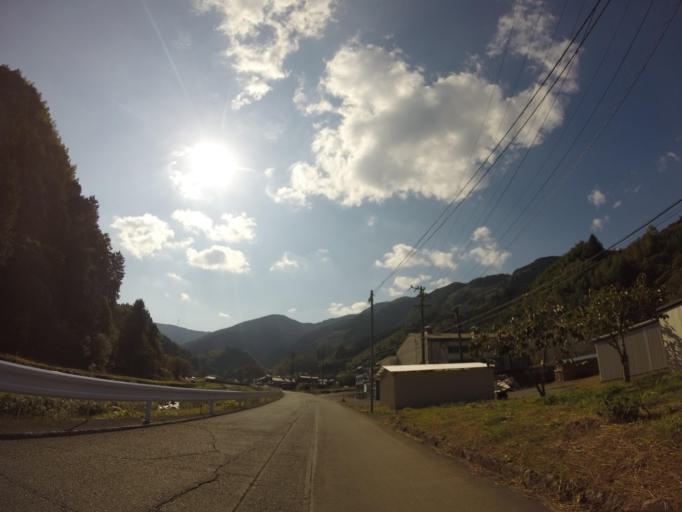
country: JP
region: Shizuoka
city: Shizuoka-shi
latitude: 35.1116
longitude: 138.4501
